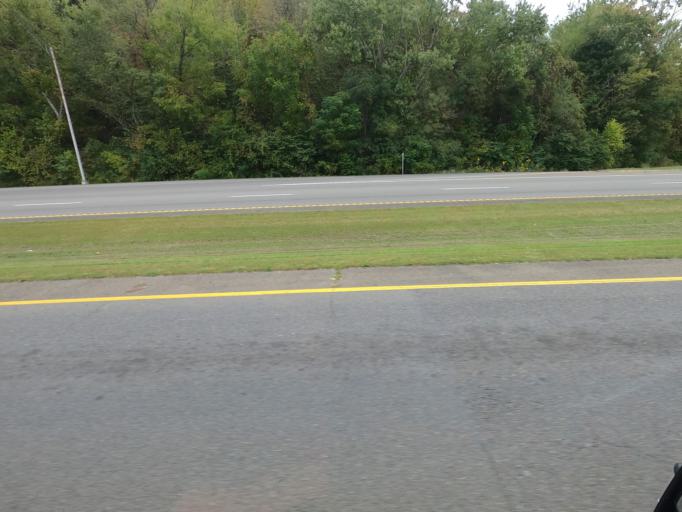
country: US
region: Tennessee
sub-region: Carter County
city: Elizabethton
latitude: 36.3446
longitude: -82.2073
